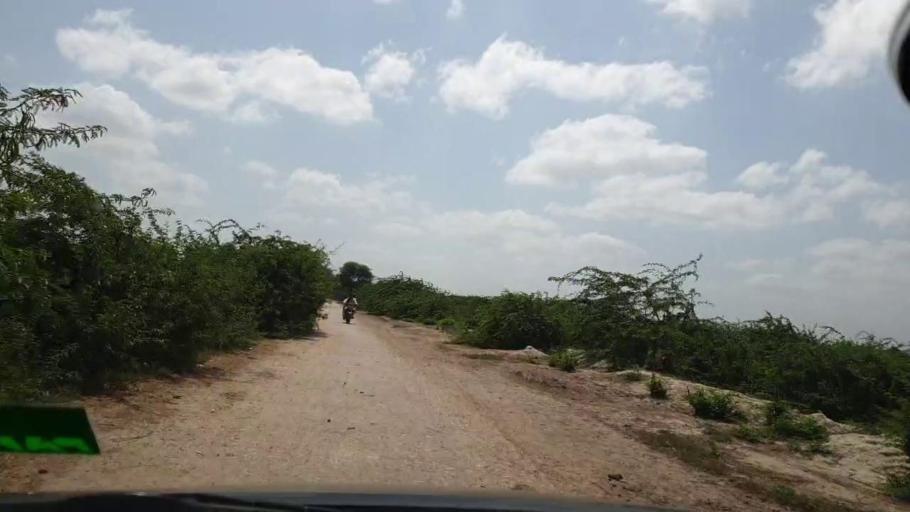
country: PK
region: Sindh
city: Kadhan
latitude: 24.5629
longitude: 69.2111
